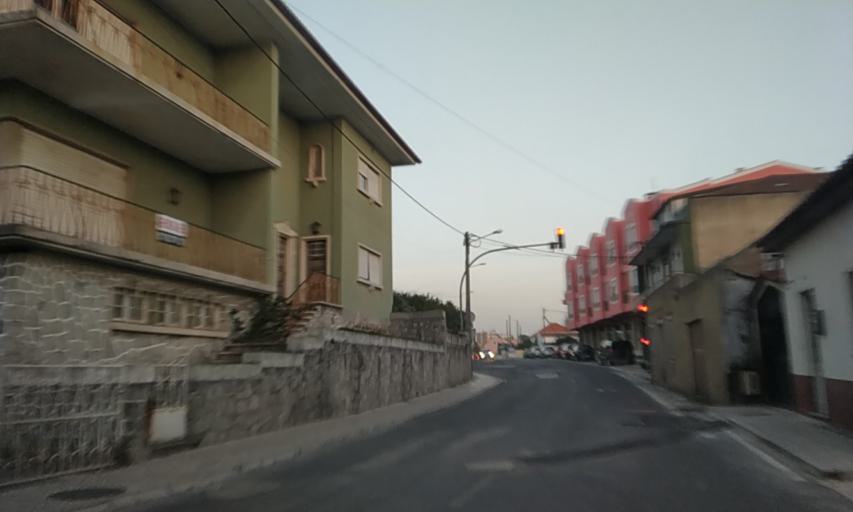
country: PT
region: Leiria
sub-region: Marinha Grande
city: Marinha Grande
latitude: 39.7509
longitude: -8.9280
